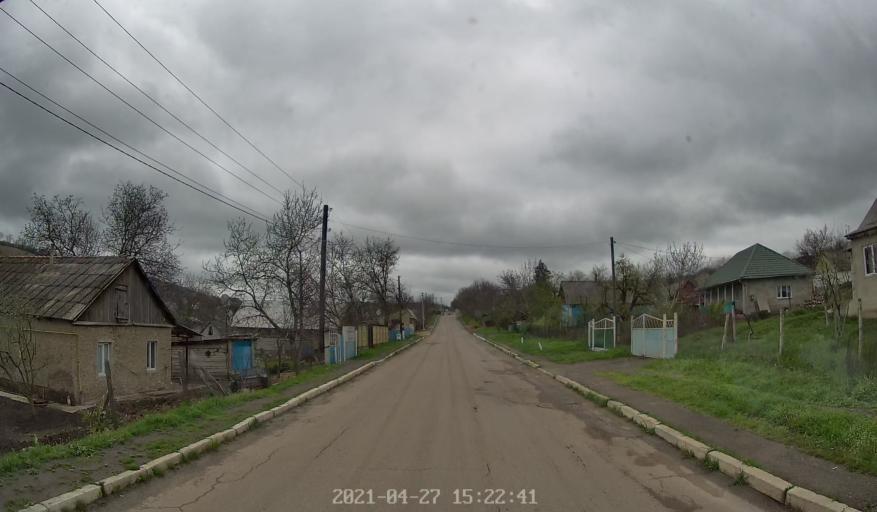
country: MD
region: Chisinau
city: Vadul lui Voda
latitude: 47.0270
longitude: 29.0247
